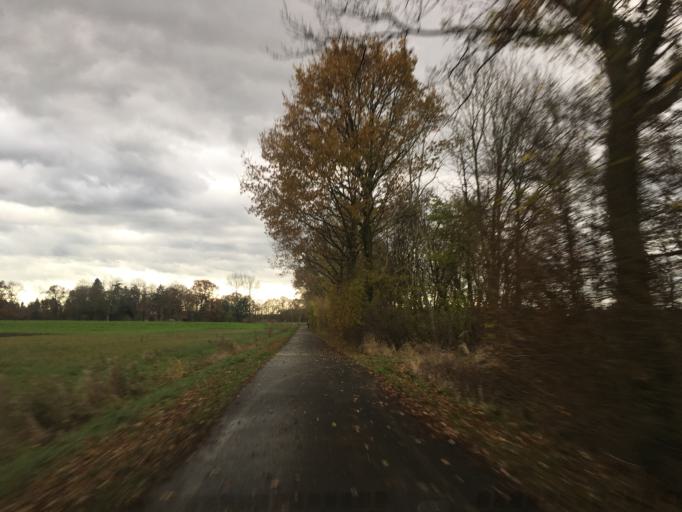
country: DE
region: North Rhine-Westphalia
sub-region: Regierungsbezirk Munster
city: Greven
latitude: 52.0290
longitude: 7.5524
